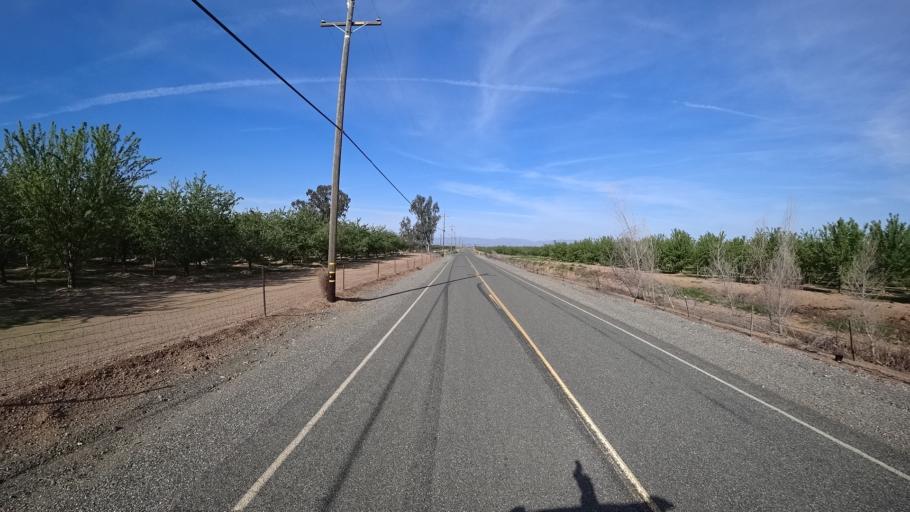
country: US
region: California
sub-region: Glenn County
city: Orland
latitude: 39.6682
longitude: -122.2516
